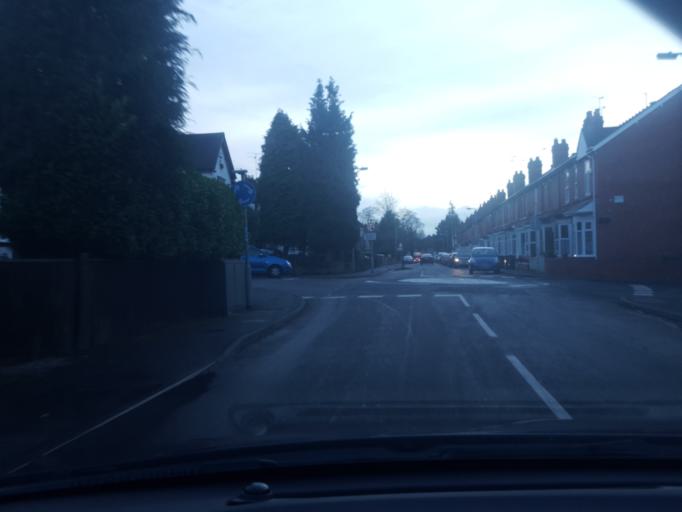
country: GB
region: England
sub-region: Wolverhampton
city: Wolverhampton
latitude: 52.5976
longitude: -2.1555
